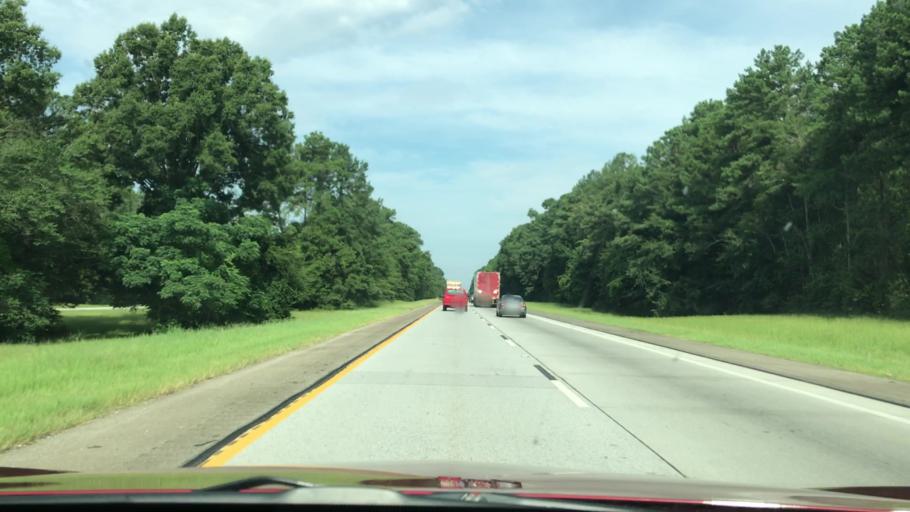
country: US
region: Georgia
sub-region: Columbia County
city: Appling
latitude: 33.5019
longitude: -82.3575
